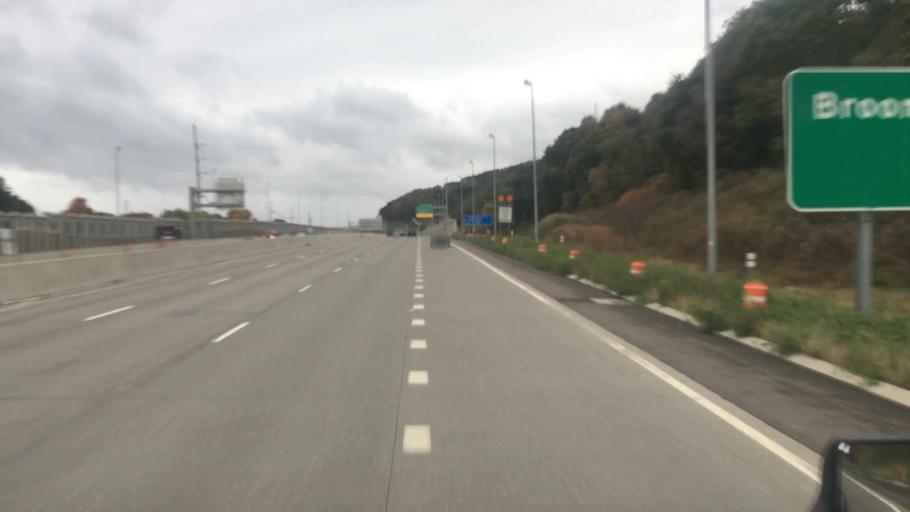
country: US
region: New York
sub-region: Broome County
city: Binghamton
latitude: 42.1122
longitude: -75.9170
